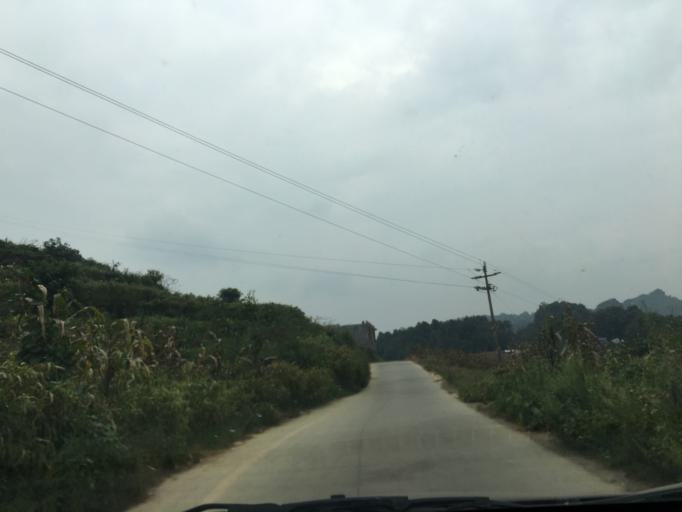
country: CN
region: Guangxi Zhuangzu Zizhiqu
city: Xinzhou
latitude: 25.5357
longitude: 105.6181
